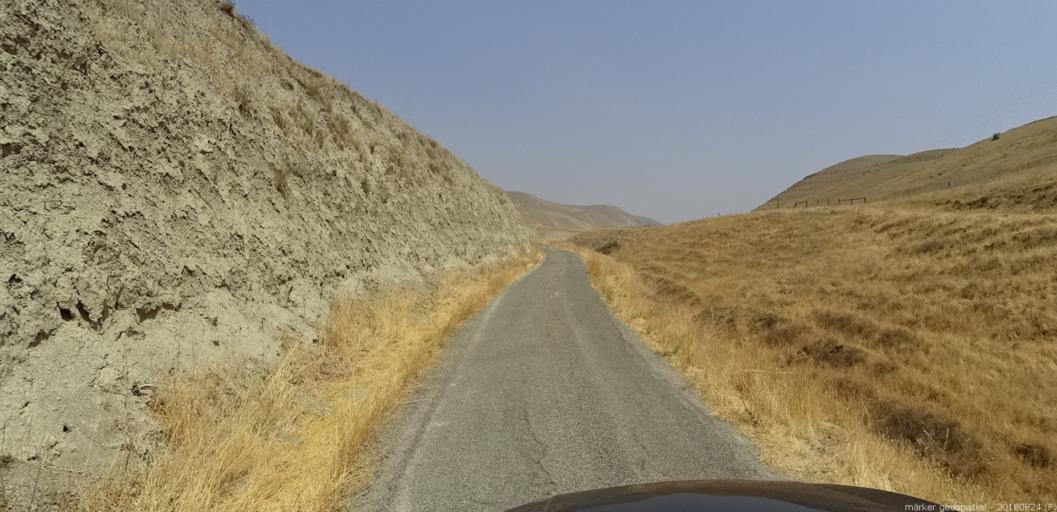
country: US
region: California
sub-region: Monterey County
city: King City
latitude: 36.1935
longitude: -120.9555
